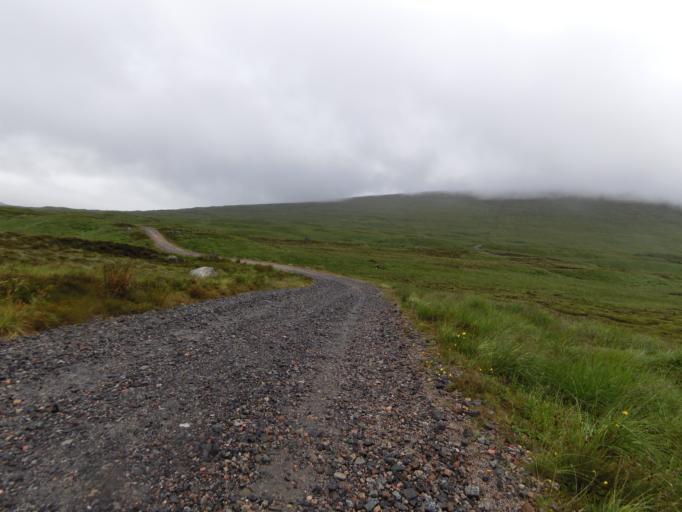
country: GB
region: Scotland
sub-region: Highland
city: Spean Bridge
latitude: 56.7655
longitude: -4.6717
